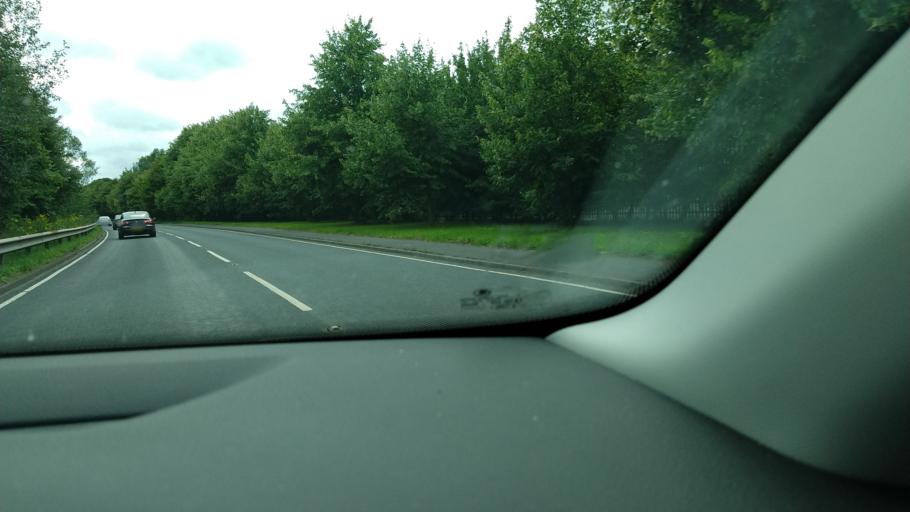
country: GB
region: England
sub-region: North Yorkshire
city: Camblesforth
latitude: 53.7293
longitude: -1.0002
